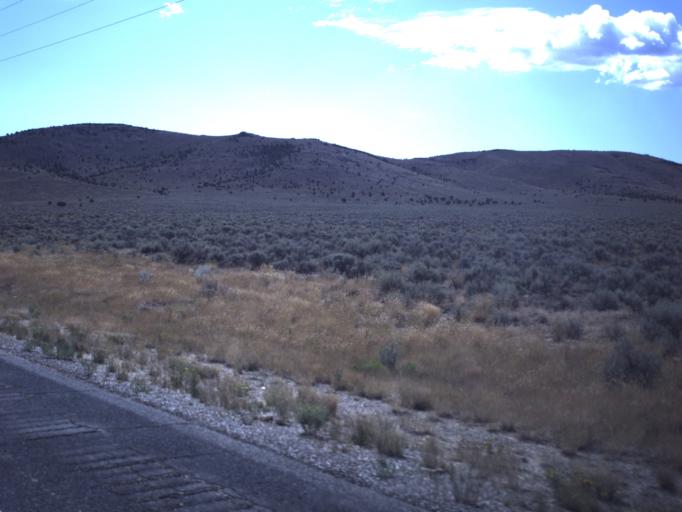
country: US
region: Utah
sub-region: Utah County
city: Eagle Mountain
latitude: 40.0748
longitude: -112.3833
